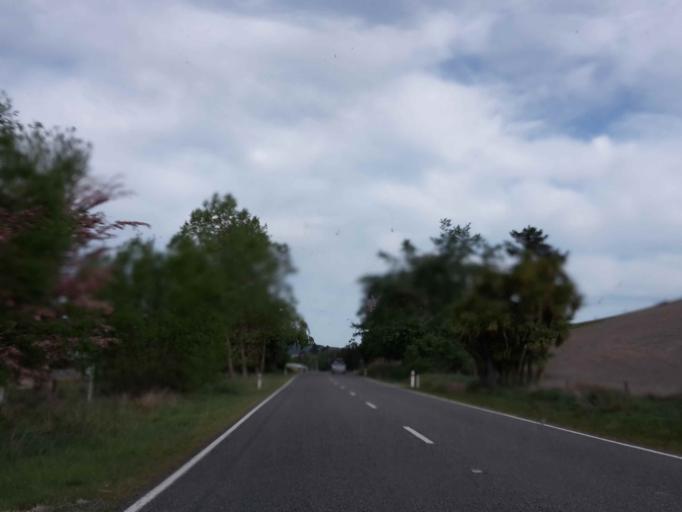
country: NZ
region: Canterbury
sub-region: Timaru District
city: Pleasant Point
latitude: -44.1058
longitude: 171.0067
